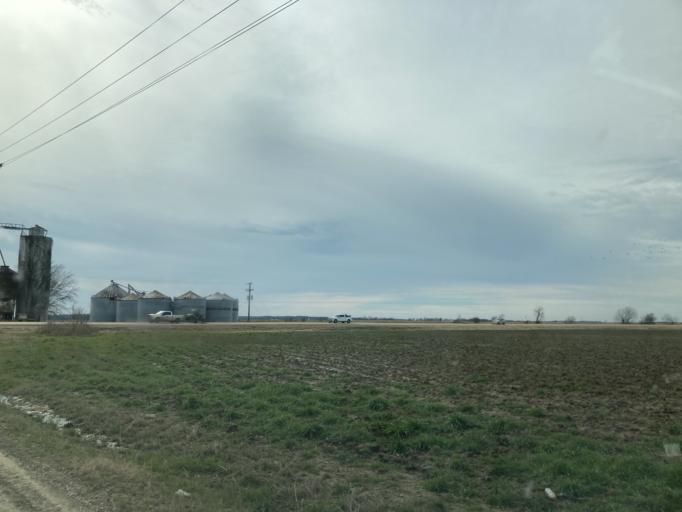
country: US
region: Mississippi
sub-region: Washington County
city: Hollandale
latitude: 33.1845
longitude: -90.6887
